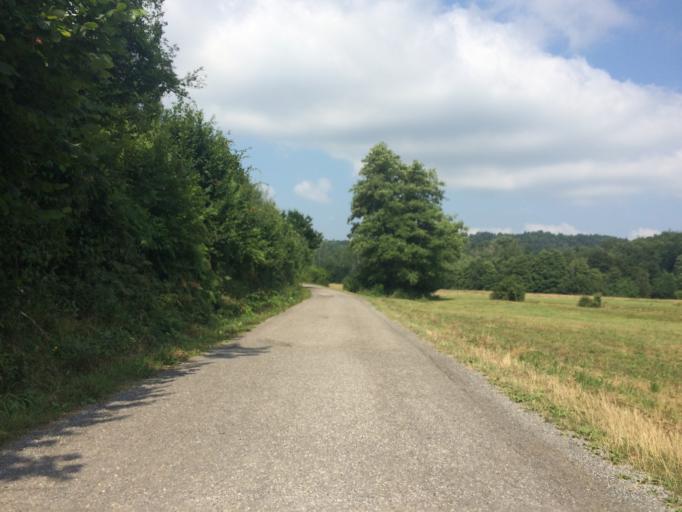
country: IT
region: Liguria
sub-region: Provincia di Savona
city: Giusvalla
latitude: 44.4625
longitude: 8.3548
